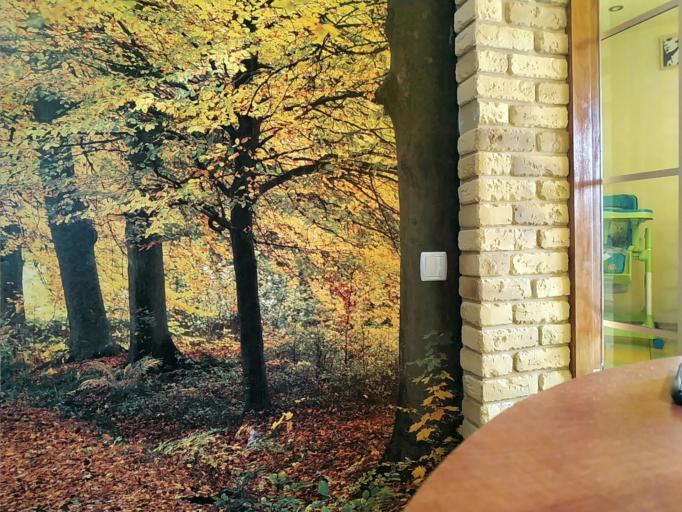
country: RU
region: Novgorod
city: Parfino
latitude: 57.7991
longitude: 31.6175
